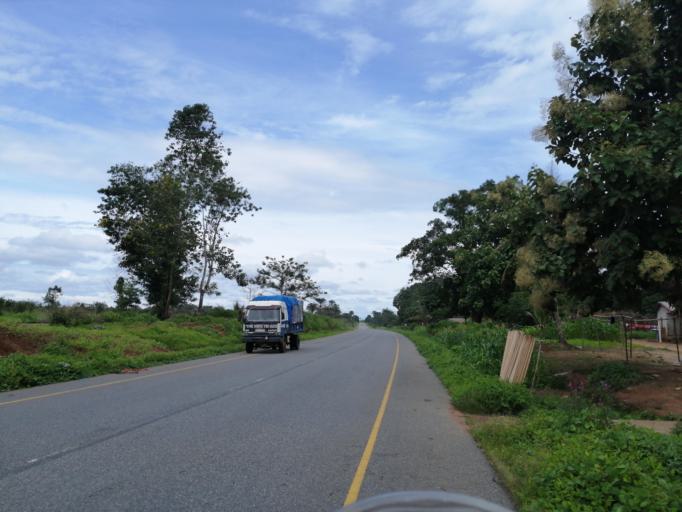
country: SL
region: Northern Province
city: Port Loko
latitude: 8.7418
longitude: -12.9392
